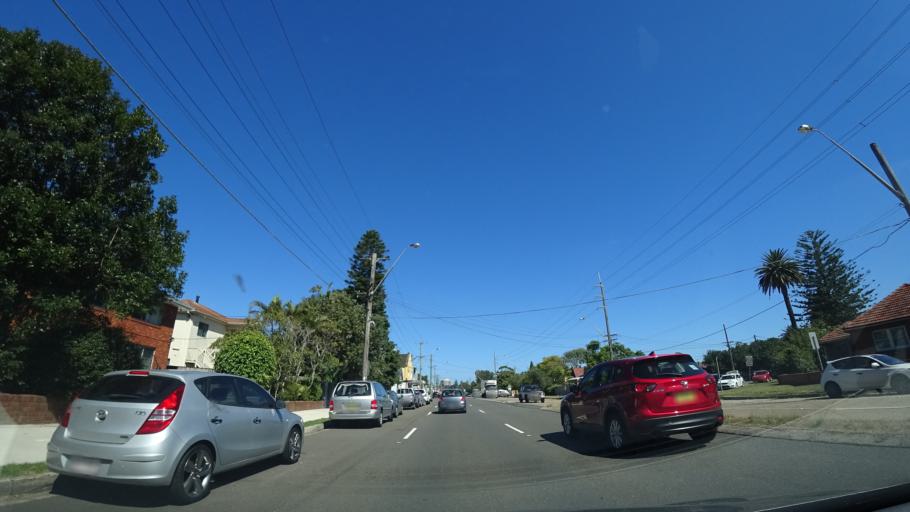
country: AU
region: New South Wales
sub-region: Warringah
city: North Manly
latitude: -33.7796
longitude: 151.2756
